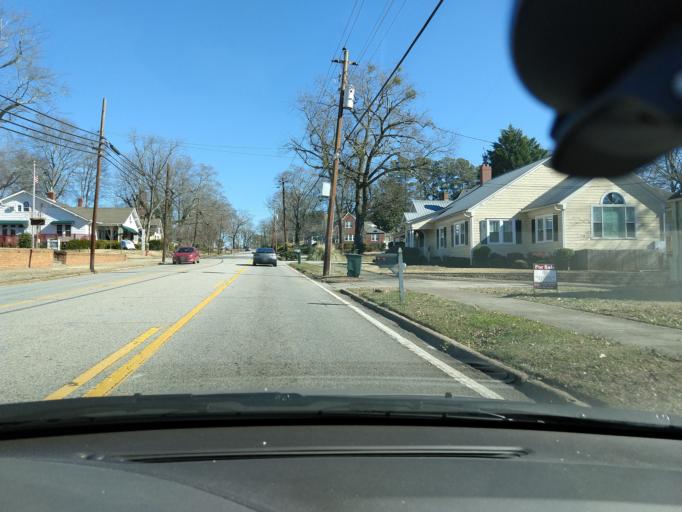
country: US
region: Georgia
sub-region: Stephens County
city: Toccoa
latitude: 34.5803
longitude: -83.3246
